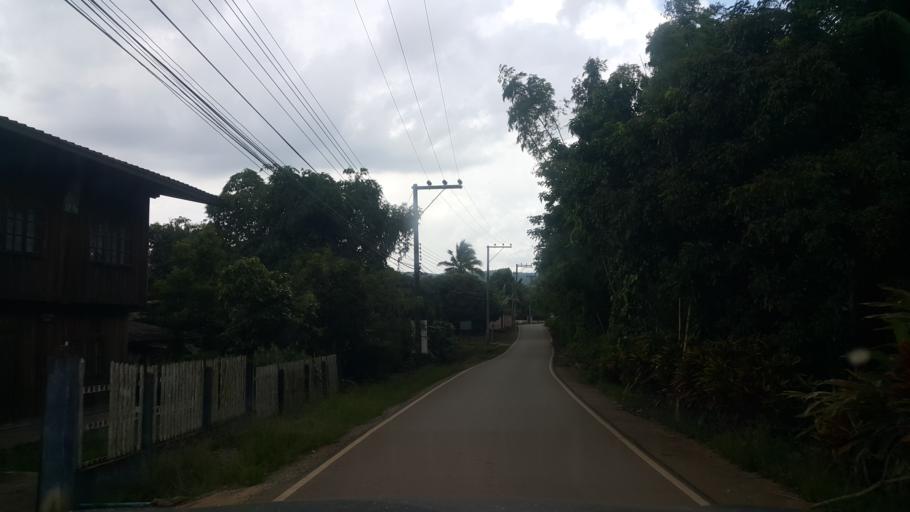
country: TH
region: Chiang Mai
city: Mae Taeng
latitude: 19.1973
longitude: 99.0014
